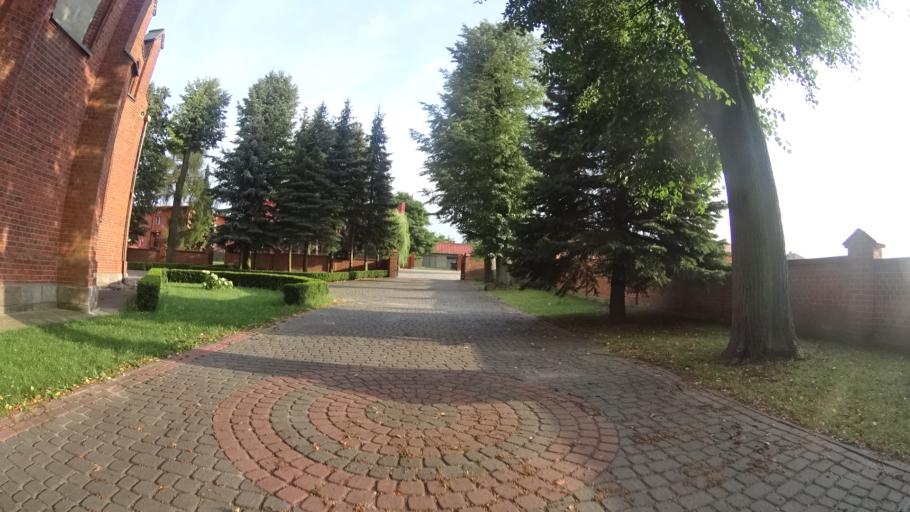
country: PL
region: Masovian Voivodeship
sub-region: Powiat grojecki
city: Mogielnica
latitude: 51.6932
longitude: 20.7206
